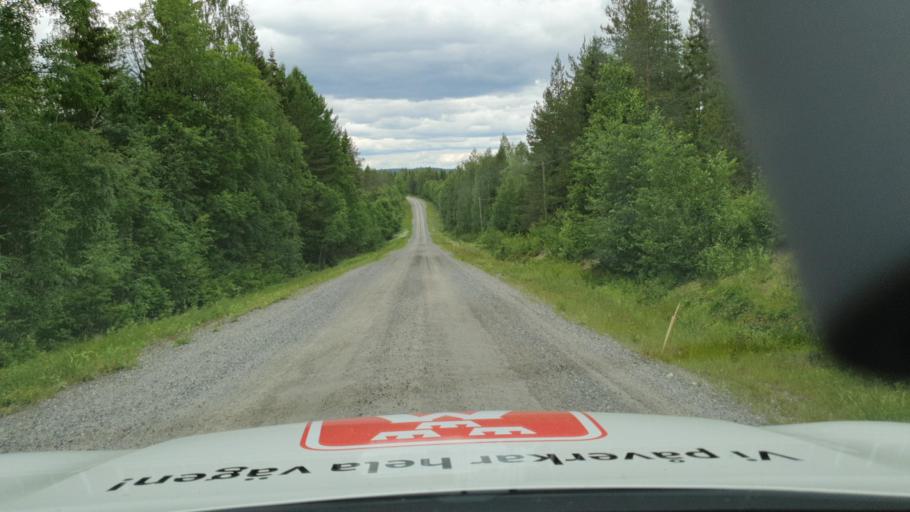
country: SE
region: Vaesterbotten
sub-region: Bjurholms Kommun
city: Bjurholm
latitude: 63.7650
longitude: 19.3369
